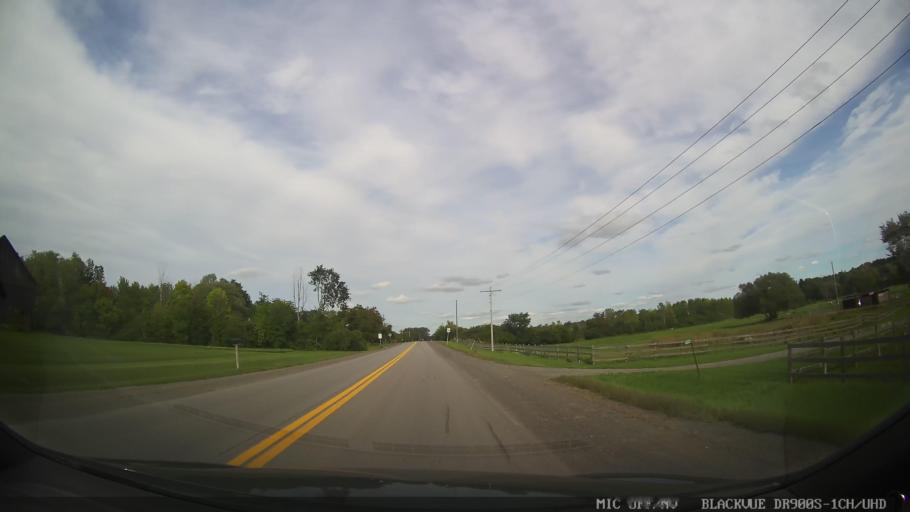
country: CA
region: Ontario
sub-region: Lanark County
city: Smiths Falls
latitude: 44.9855
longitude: -75.7896
